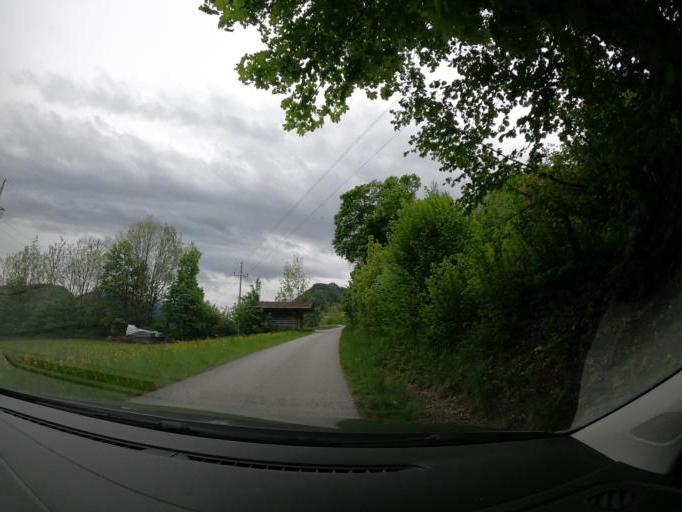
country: AT
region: Salzburg
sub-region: Politischer Bezirk Sankt Johann im Pongau
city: Werfen
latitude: 47.4659
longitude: 13.1941
